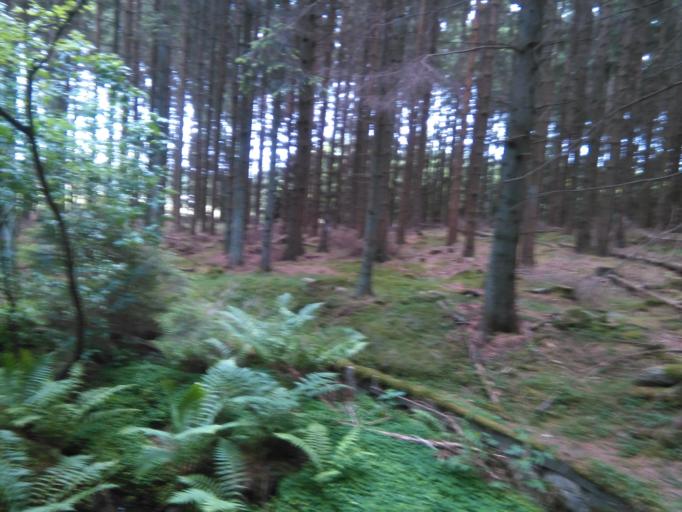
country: DK
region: Capital Region
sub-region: Bornholm Kommune
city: Akirkeby
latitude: 55.1099
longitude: 14.9437
